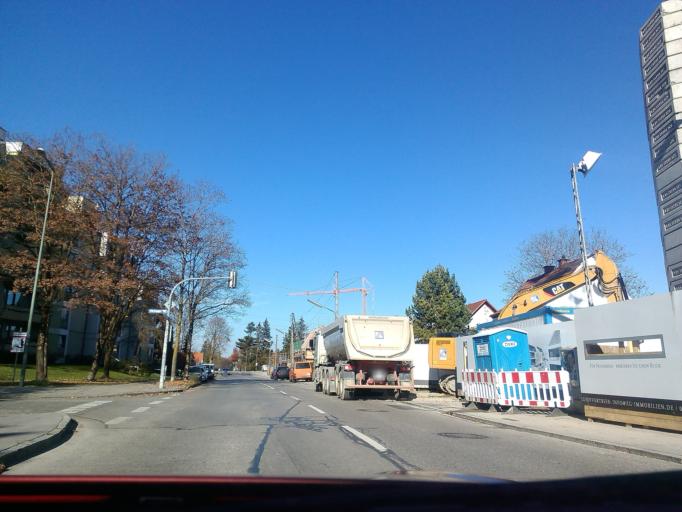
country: DE
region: Bavaria
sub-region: Upper Bavaria
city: Germering
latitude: 48.1643
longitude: 11.4133
